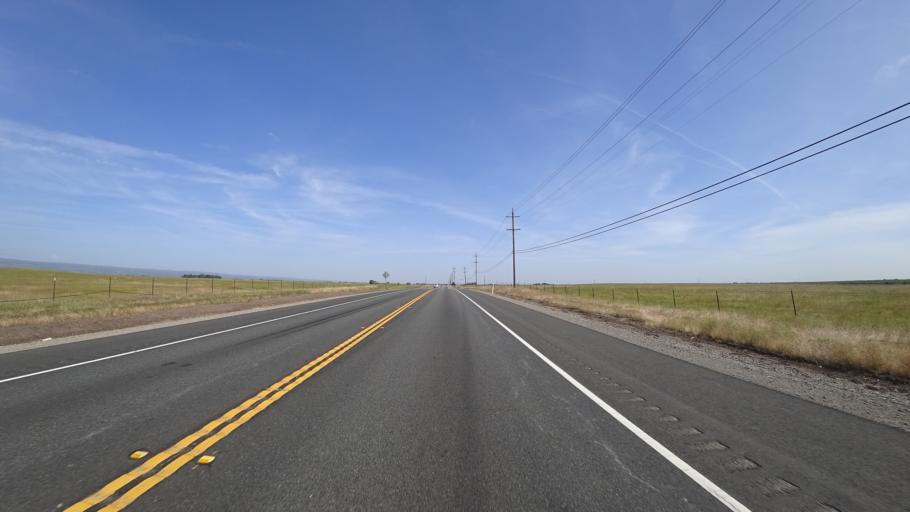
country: US
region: California
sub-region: Glenn County
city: Hamilton City
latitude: 39.8693
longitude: -121.9659
